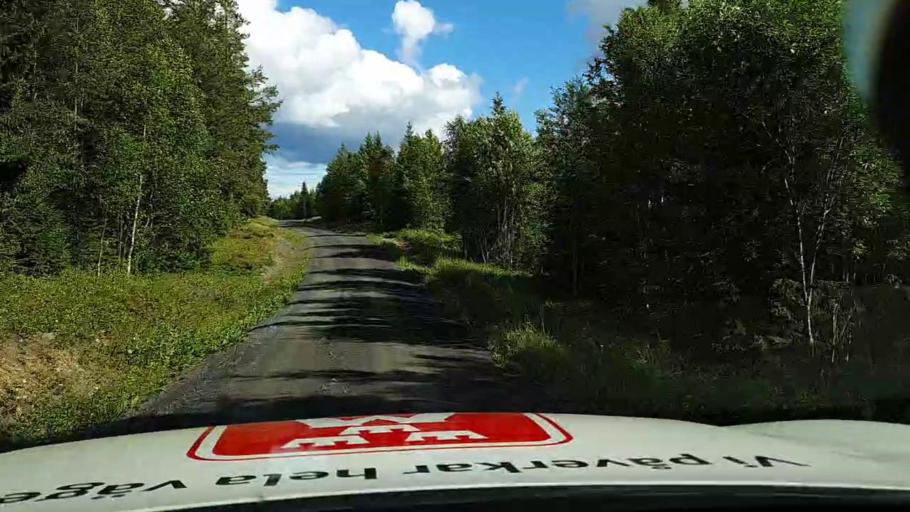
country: SE
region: Jaemtland
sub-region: Krokoms Kommun
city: Valla
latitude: 63.3255
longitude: 13.7423
